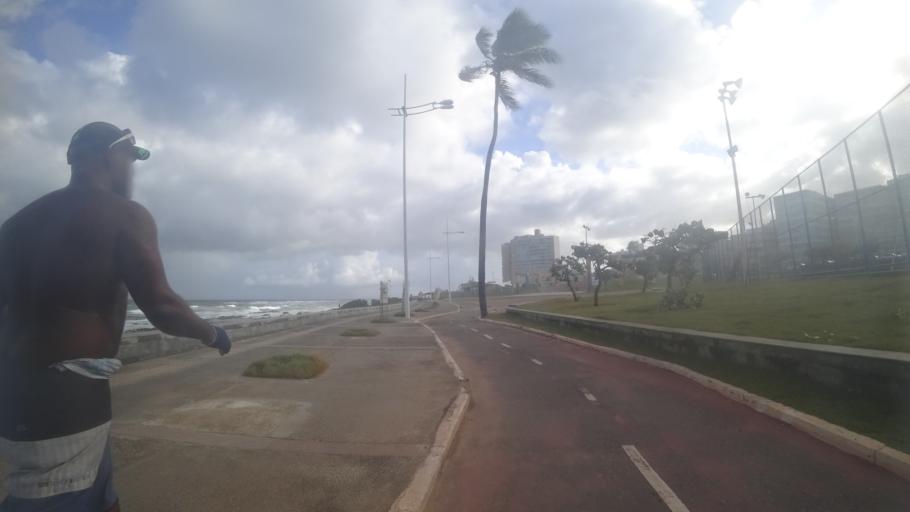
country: BR
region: Bahia
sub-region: Salvador
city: Salvador
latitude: -13.0025
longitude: -38.4503
